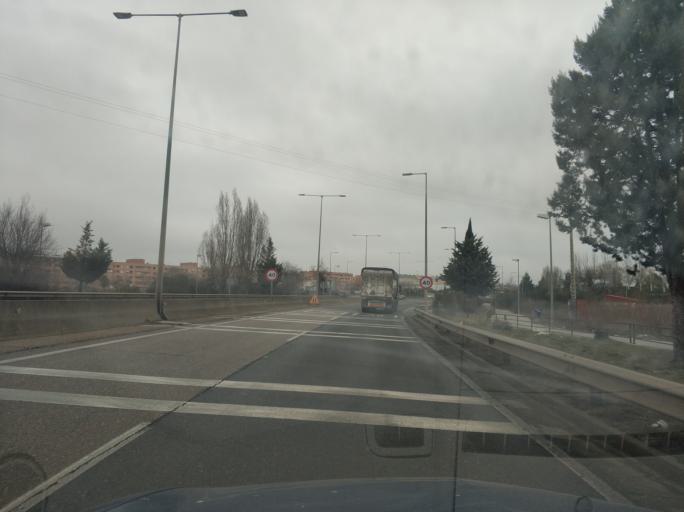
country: ES
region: Castille and Leon
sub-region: Provincia de Valladolid
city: Valladolid
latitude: 41.6398
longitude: -4.7028
